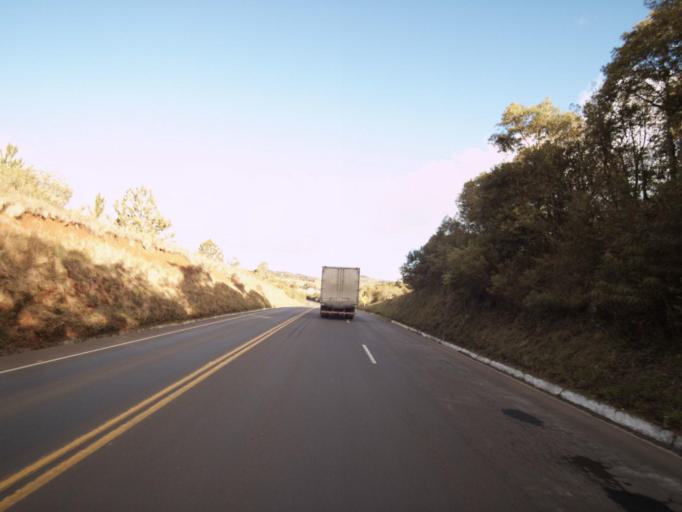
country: BR
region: Santa Catarina
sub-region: Campos Novos
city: Campos Novos
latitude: -27.3412
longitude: -51.3410
